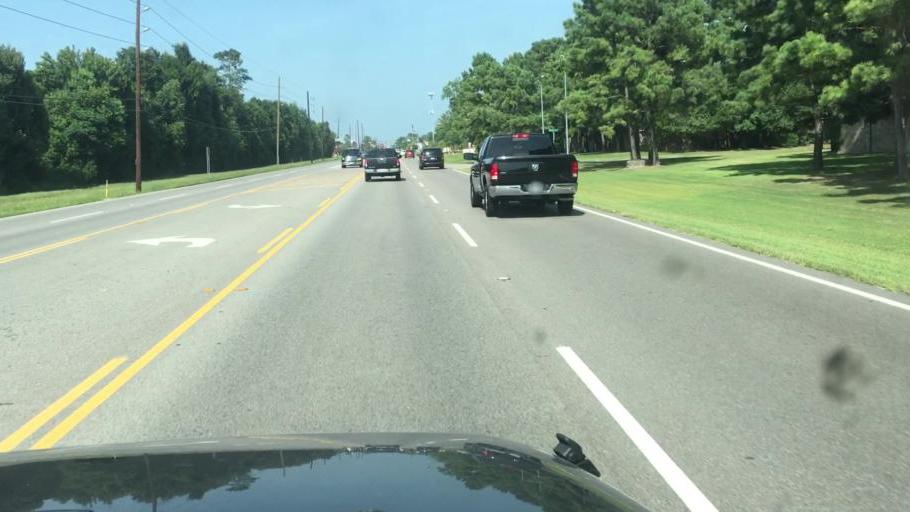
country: US
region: Texas
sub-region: Harris County
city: Atascocita
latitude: 29.9917
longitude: -95.1828
